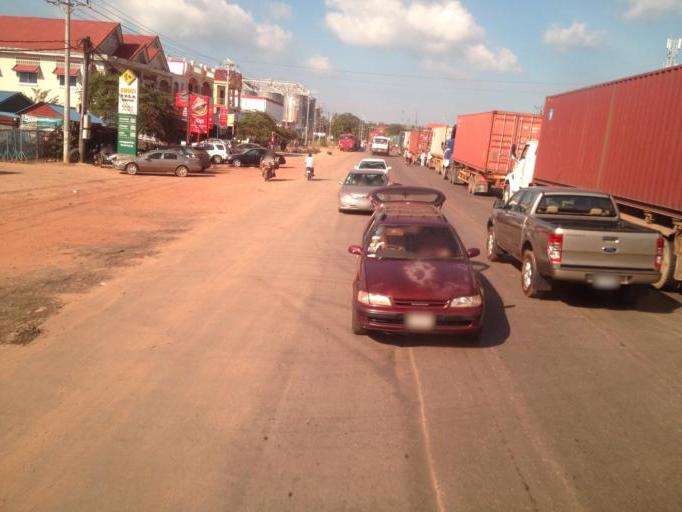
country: KH
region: Preah Sihanouk
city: Sihanoukville
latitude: 10.6348
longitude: 103.5371
